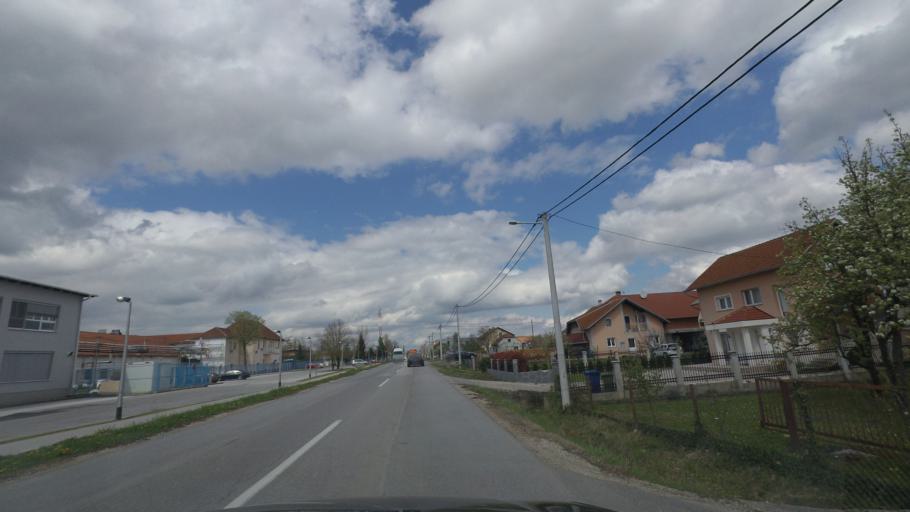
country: HR
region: Zagrebacka
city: Kerestinec
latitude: 45.7647
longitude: 15.8048
